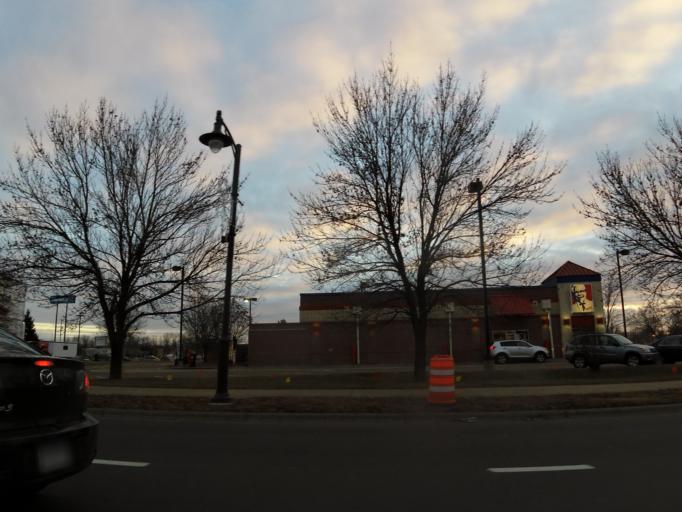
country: US
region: Minnesota
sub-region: Ramsey County
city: Vadnais Heights
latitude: 45.0503
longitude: -93.0619
